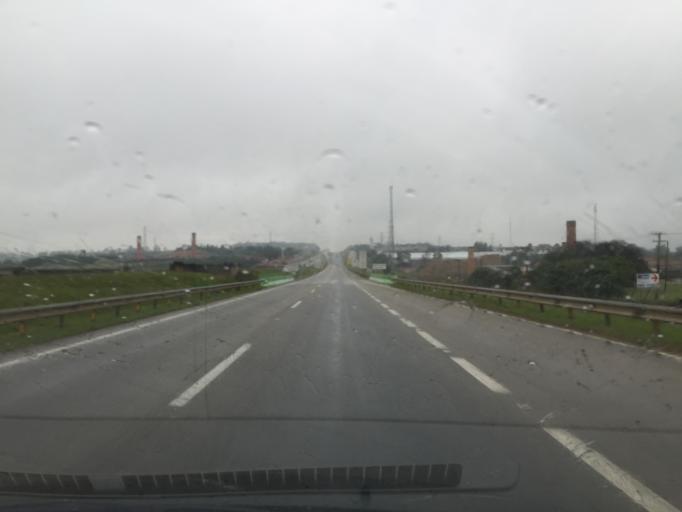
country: BR
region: Sao Paulo
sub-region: Itu
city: Itu
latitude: -23.3139
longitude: -47.3298
